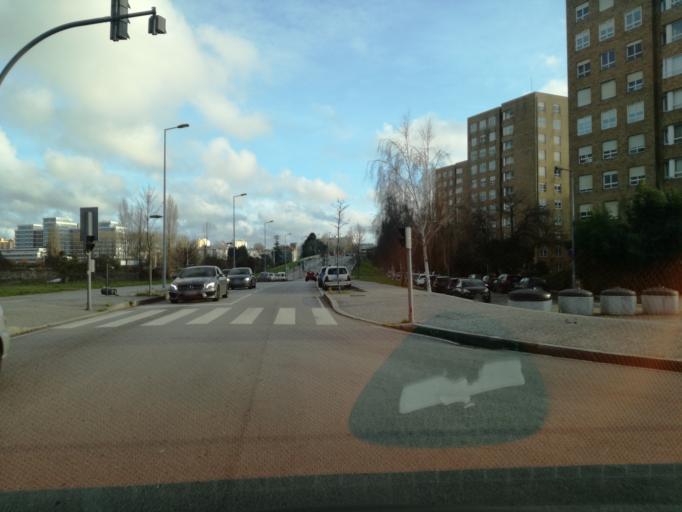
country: PT
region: Porto
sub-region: Matosinhos
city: Senhora da Hora
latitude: 41.1744
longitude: -8.6341
